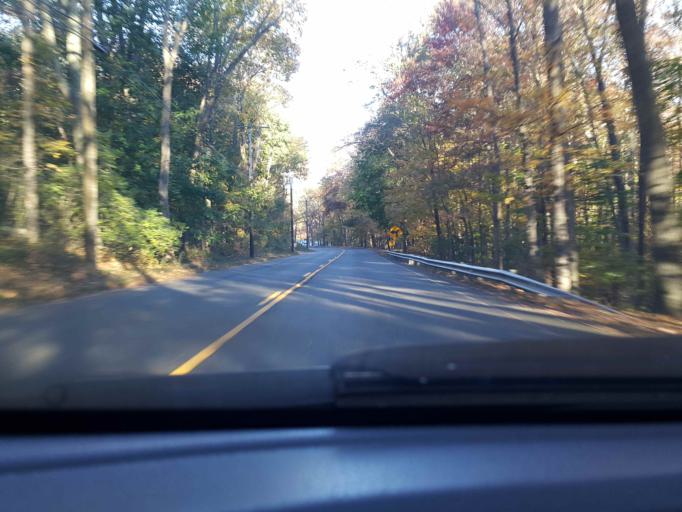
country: US
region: Connecticut
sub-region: New Haven County
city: Woodbridge
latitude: 41.3856
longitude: -73.0178
